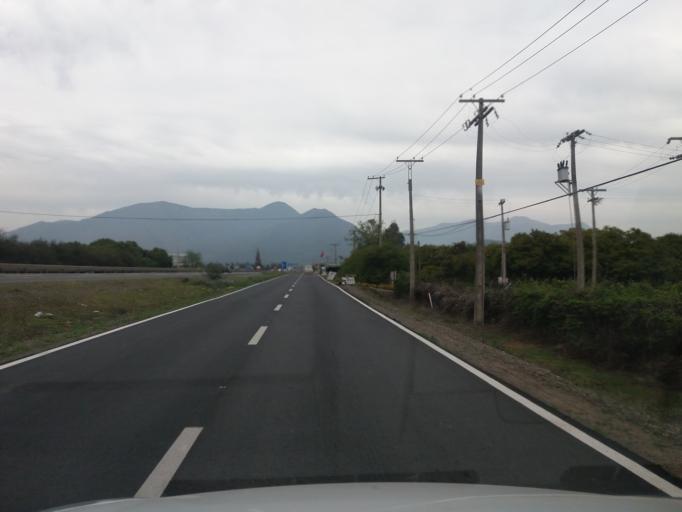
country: CL
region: Valparaiso
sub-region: Provincia de Quillota
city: Hacienda La Calera
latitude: -32.8375
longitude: -71.1163
